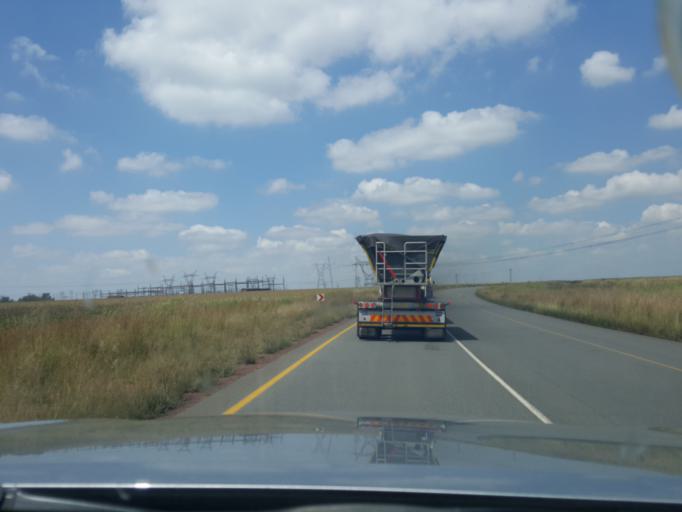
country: ZA
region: Mpumalanga
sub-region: Nkangala District Municipality
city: Witbank
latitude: -26.0142
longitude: 29.4159
